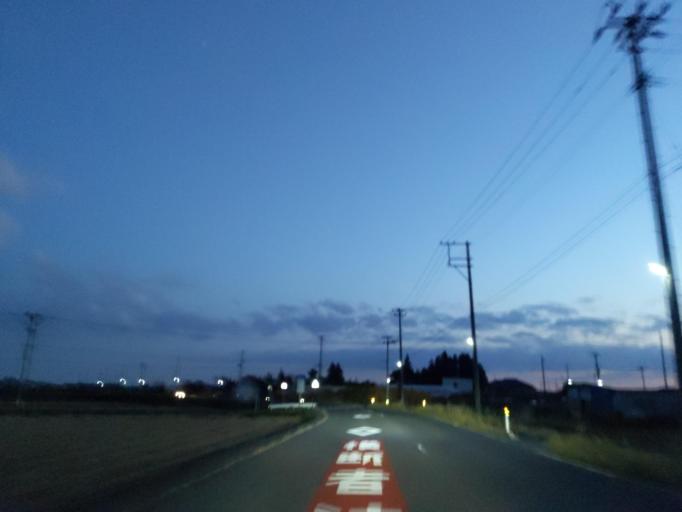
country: JP
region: Fukushima
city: Koriyama
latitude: 37.4352
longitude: 140.3121
